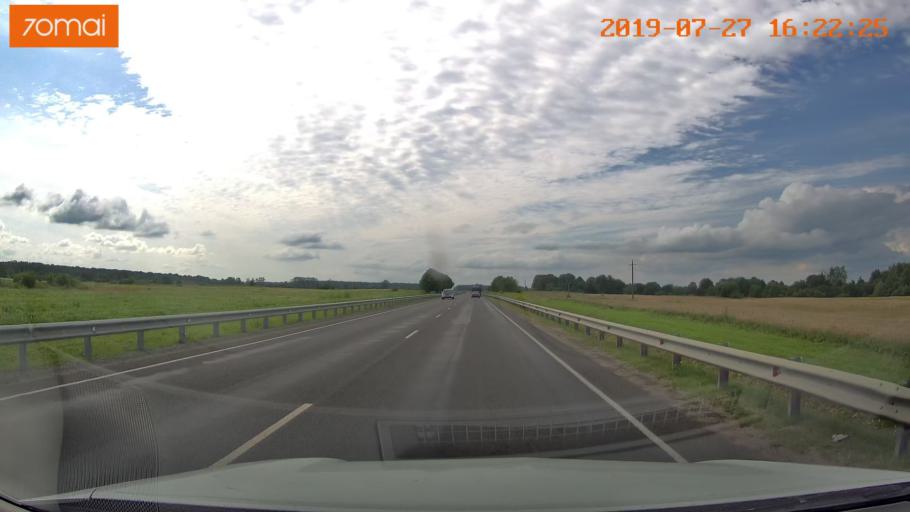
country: RU
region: Kaliningrad
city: Chernyakhovsk
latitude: 54.6281
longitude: 21.4952
